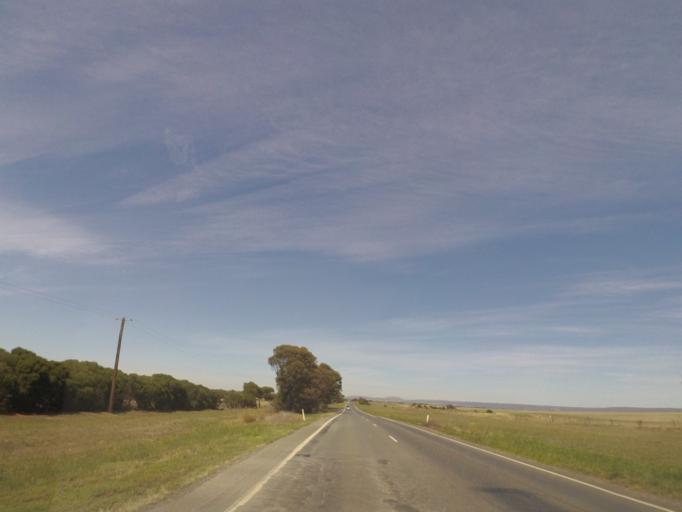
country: AU
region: Victoria
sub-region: Moorabool
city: Bacchus Marsh
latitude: -37.7828
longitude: 144.4289
